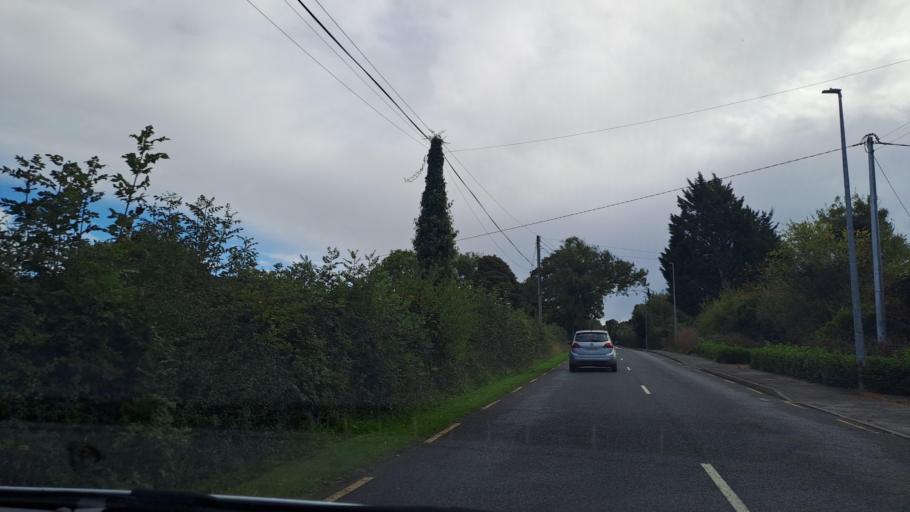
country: IE
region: Ulster
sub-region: County Monaghan
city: Carrickmacross
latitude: 53.9624
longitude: -6.7069
